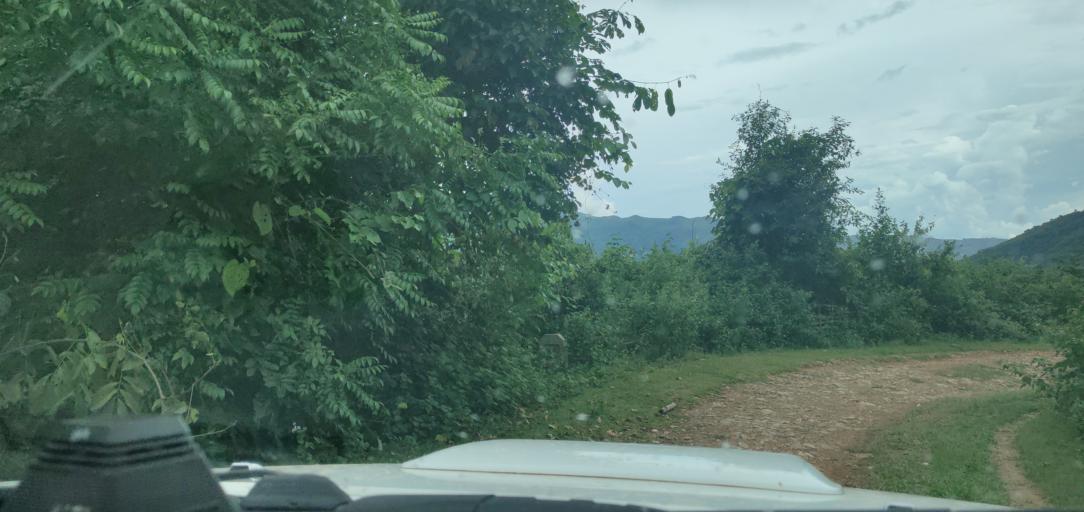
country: LA
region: Phongsali
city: Phongsali
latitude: 21.4398
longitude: 102.3294
